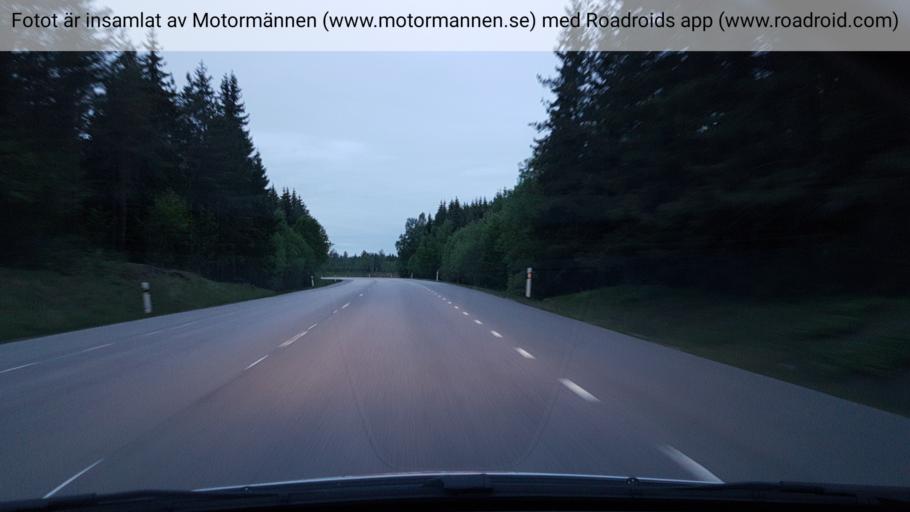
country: SE
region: Uppsala
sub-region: Heby Kommun
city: Heby
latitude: 59.9375
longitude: 16.8230
